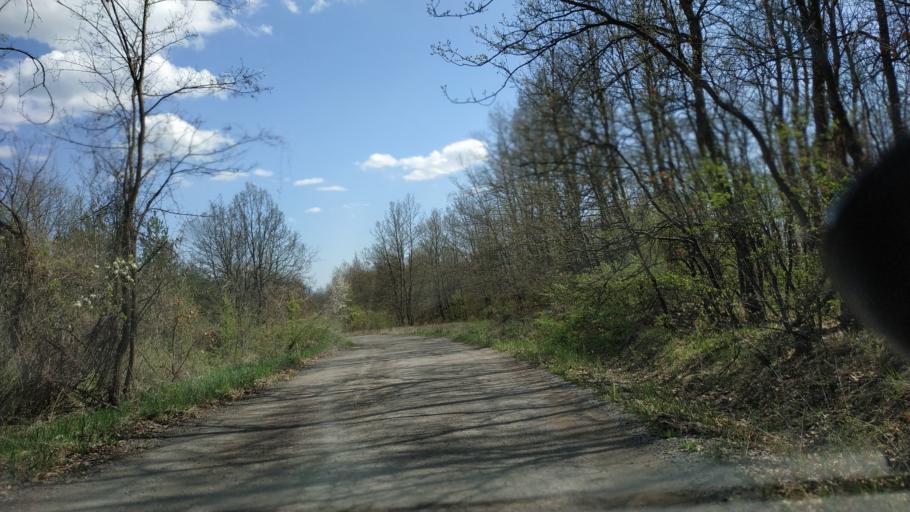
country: RS
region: Central Serbia
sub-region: Zajecarski Okrug
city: Soko Banja
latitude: 43.5400
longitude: 21.9038
